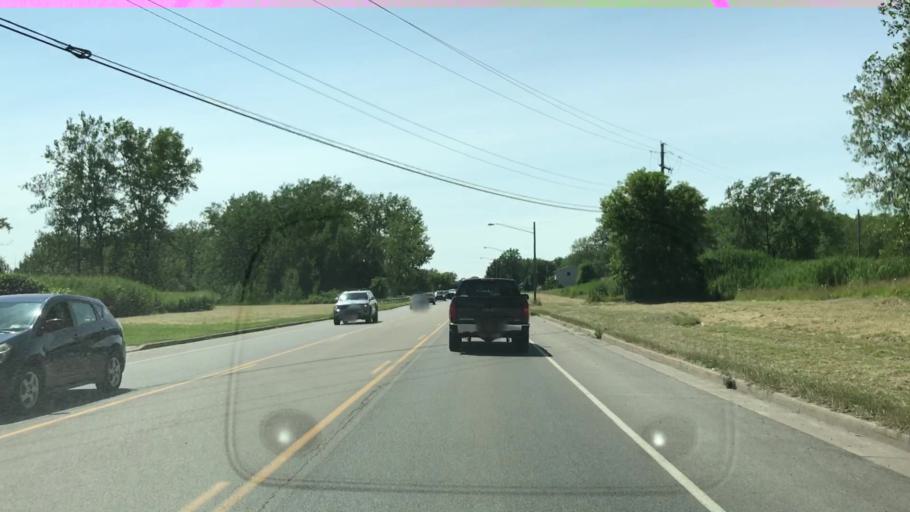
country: US
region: New York
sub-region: Erie County
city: Cheektowaga
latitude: 42.8817
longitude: -78.7367
